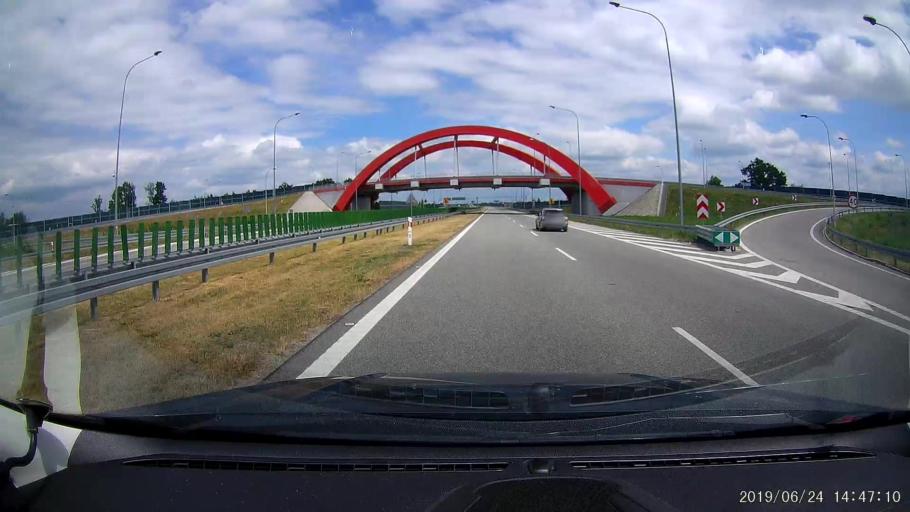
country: PL
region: Subcarpathian Voivodeship
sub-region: Powiat debicki
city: Zyrakow
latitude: 50.0787
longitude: 21.3829
